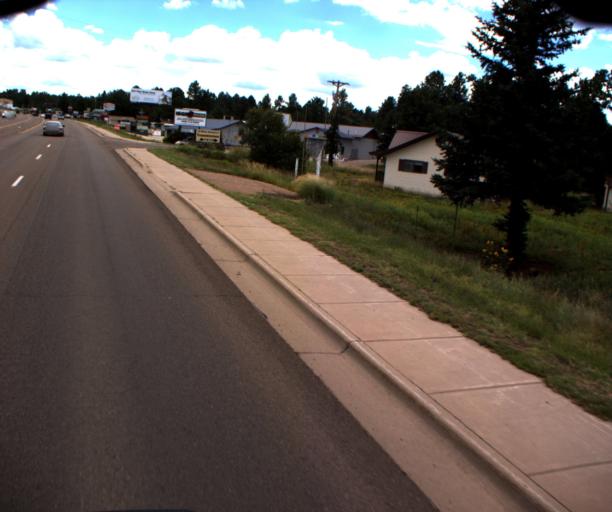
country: US
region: Arizona
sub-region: Navajo County
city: Lake of the Woods
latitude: 34.1718
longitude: -110.0031
